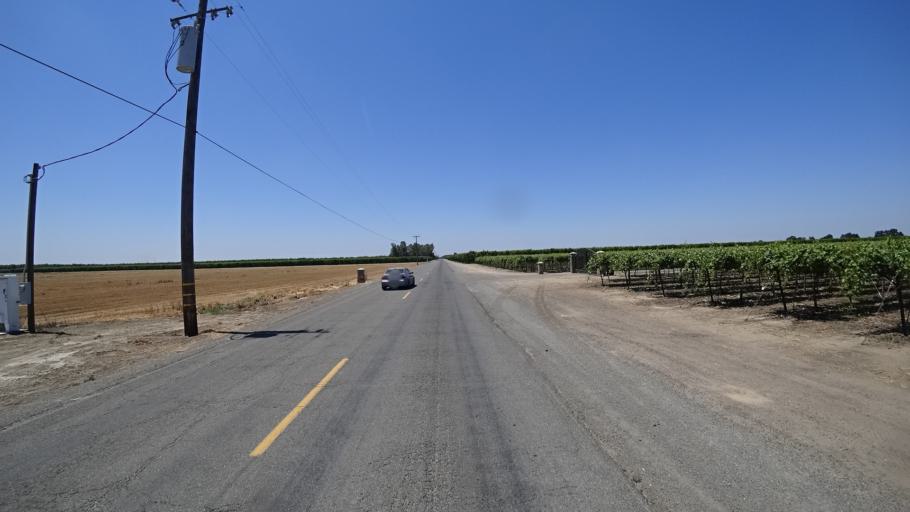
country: US
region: California
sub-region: Fresno County
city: Kingsburg
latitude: 36.4305
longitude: -119.5484
